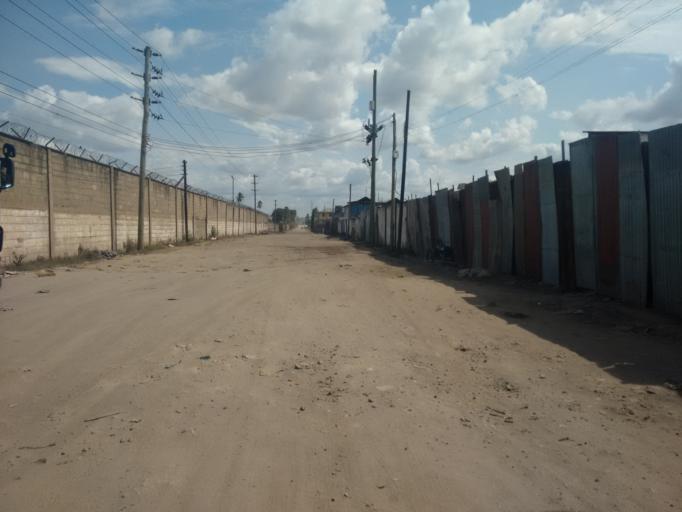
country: TZ
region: Dar es Salaam
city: Dar es Salaam
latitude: -6.8428
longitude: 39.2641
